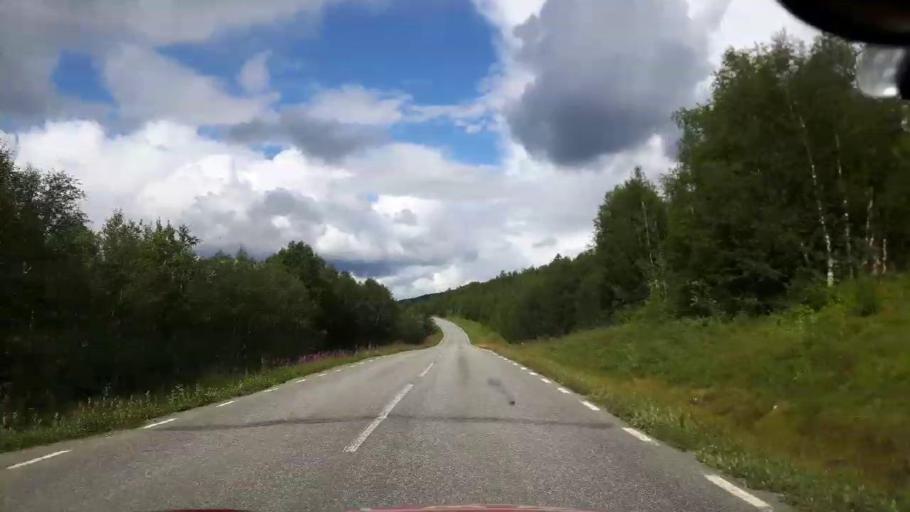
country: NO
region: Nordland
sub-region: Hattfjelldal
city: Hattfjelldal
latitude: 65.0519
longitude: 14.7404
